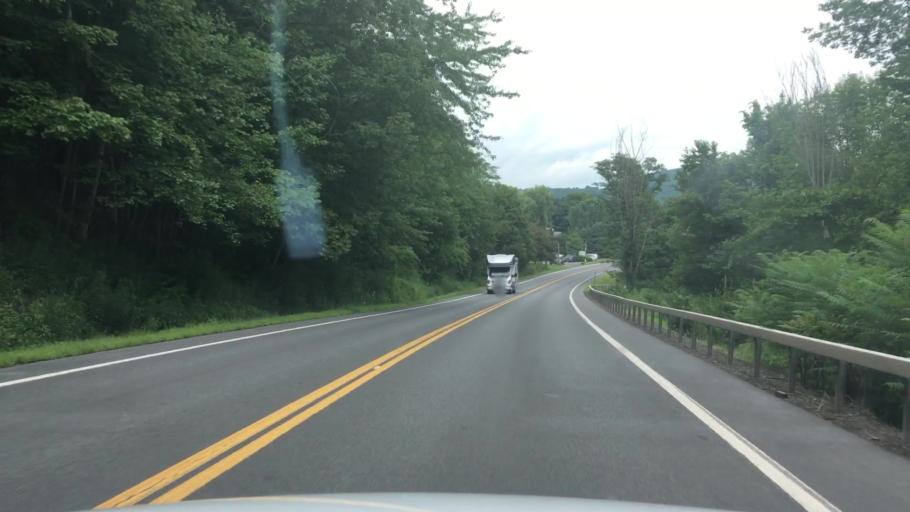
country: US
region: New York
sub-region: Otsego County
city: Otego
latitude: 42.4111
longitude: -75.1498
